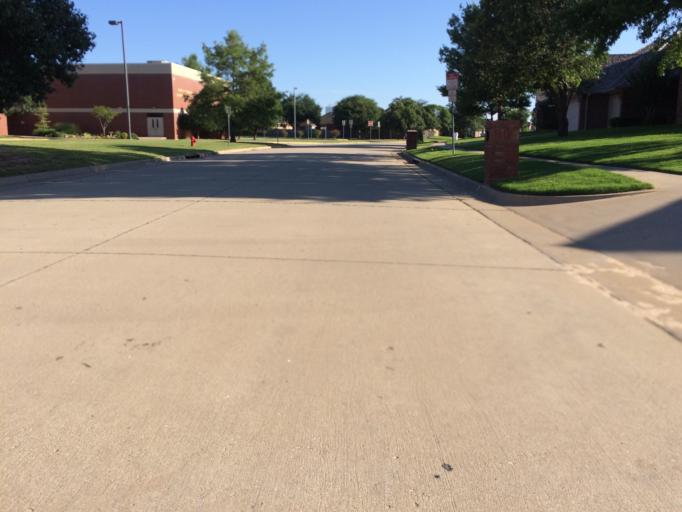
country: US
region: Oklahoma
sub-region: Cleveland County
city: Norman
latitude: 35.2266
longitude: -97.5016
